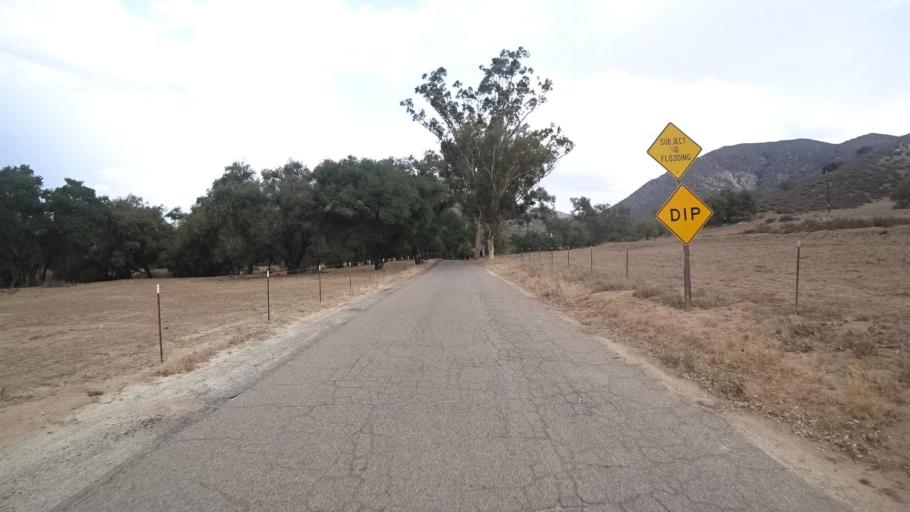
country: US
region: California
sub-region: San Diego County
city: Ramona
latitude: 33.1181
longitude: -116.8509
